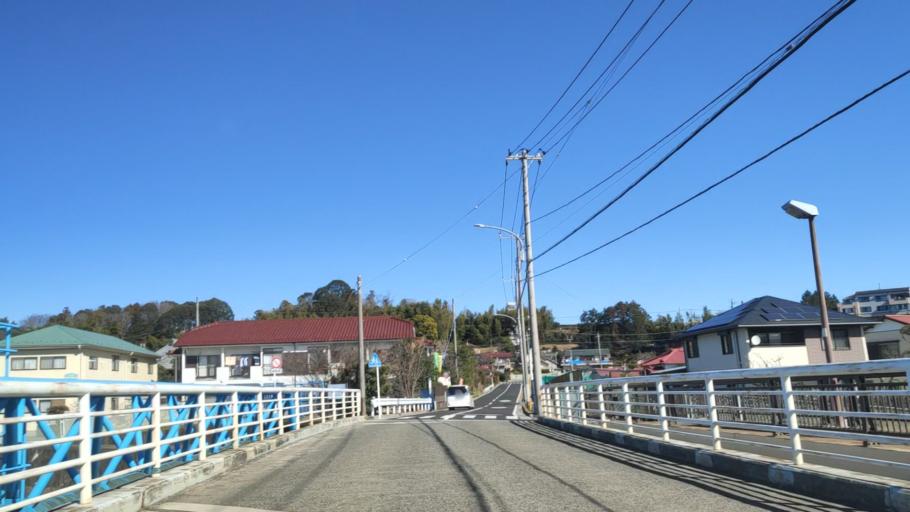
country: JP
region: Tokyo
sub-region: Machida-shi
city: Machida
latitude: 35.5189
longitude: 139.5360
